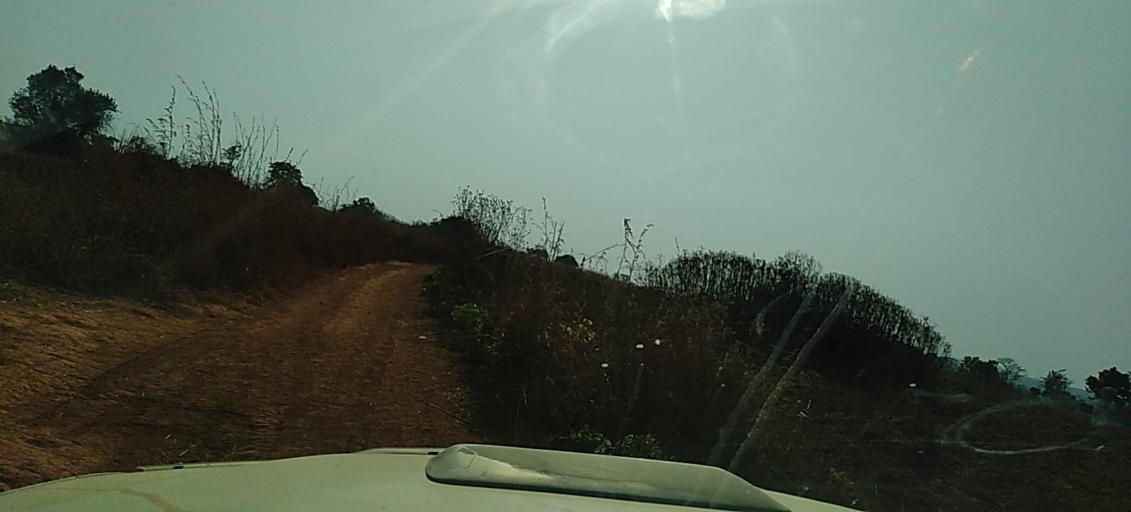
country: ZM
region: North-Western
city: Kasempa
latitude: -13.1830
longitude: 25.9483
